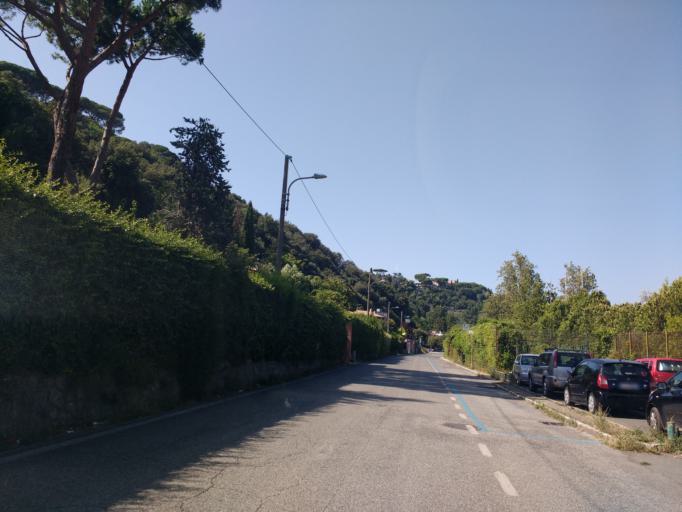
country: IT
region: Latium
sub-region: Citta metropolitana di Roma Capitale
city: Castel Gandolfo
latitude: 41.7528
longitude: 12.6511
